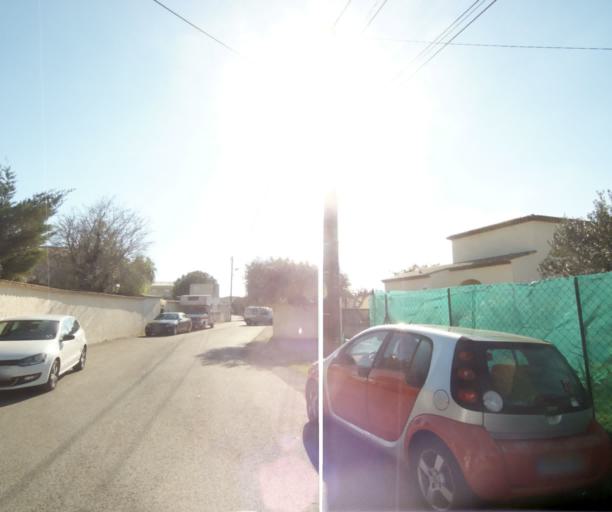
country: FR
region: Provence-Alpes-Cote d'Azur
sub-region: Departement des Alpes-Maritimes
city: Biot
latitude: 43.6082
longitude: 7.1162
